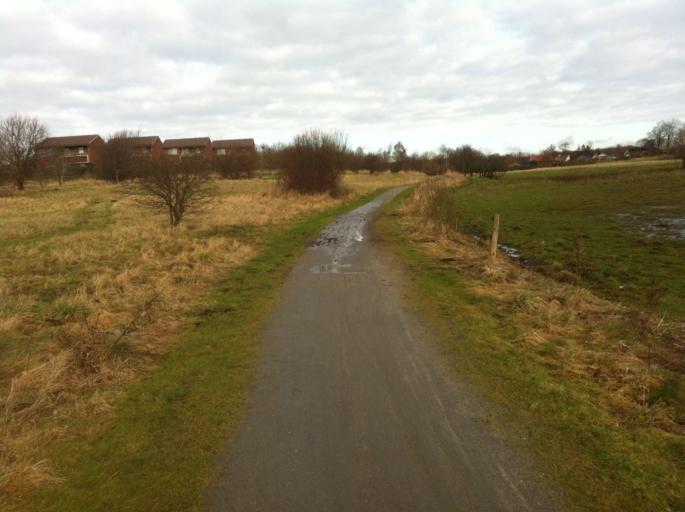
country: DK
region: South Denmark
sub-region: Odense Kommune
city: Odense
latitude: 55.4332
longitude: 10.3475
